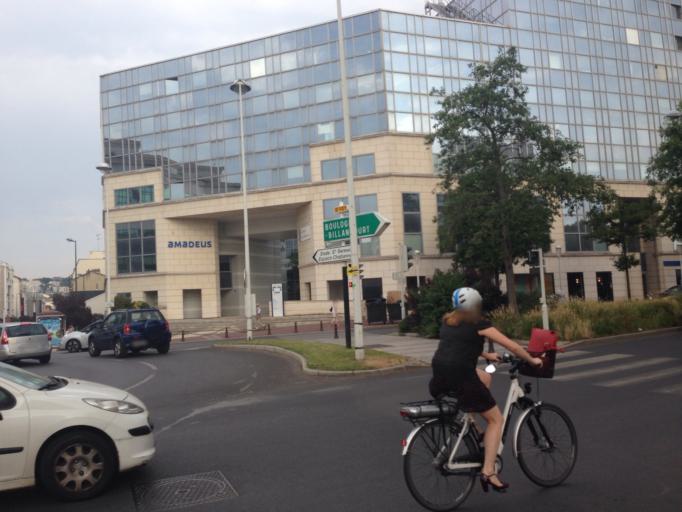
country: FR
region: Ile-de-France
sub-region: Departement des Hauts-de-Seine
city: Boulogne-Billancourt
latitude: 48.8233
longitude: 2.2497
